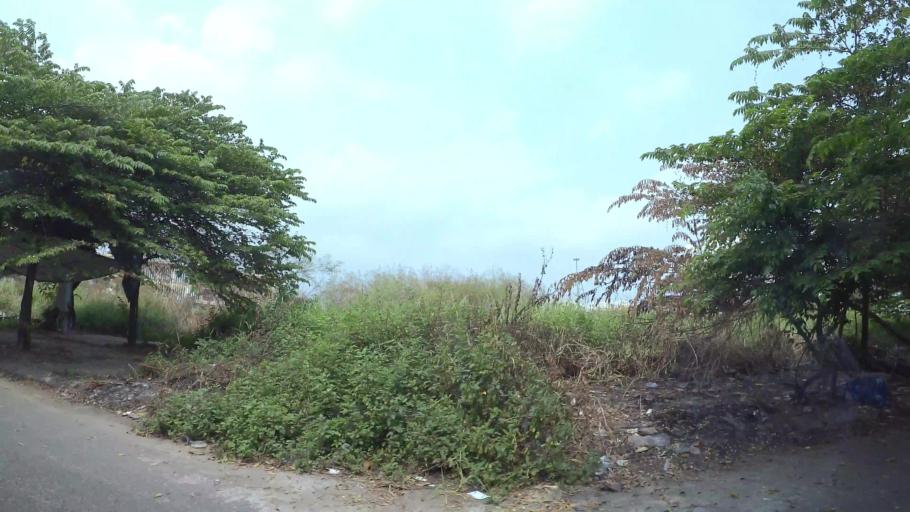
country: VN
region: Da Nang
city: Da Nang
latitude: 16.0875
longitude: 108.2336
